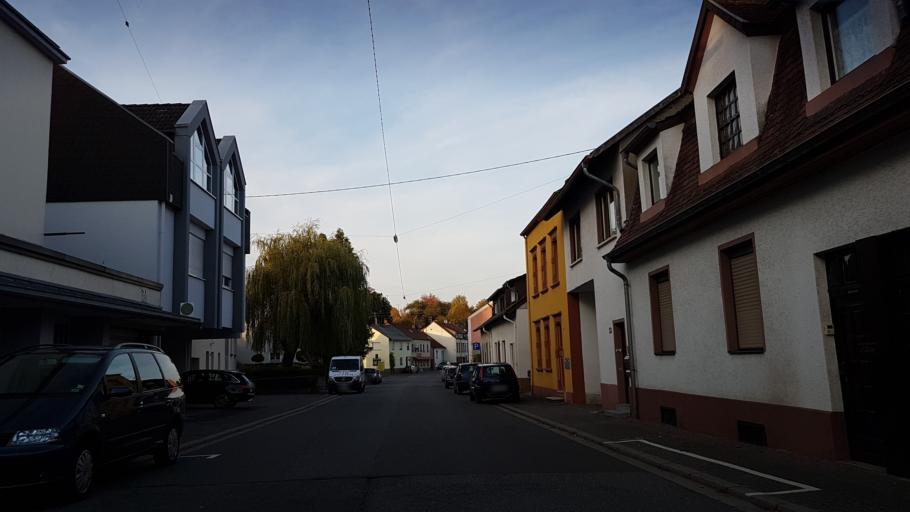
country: DE
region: Saarland
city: Lebach
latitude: 49.4128
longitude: 6.9128
